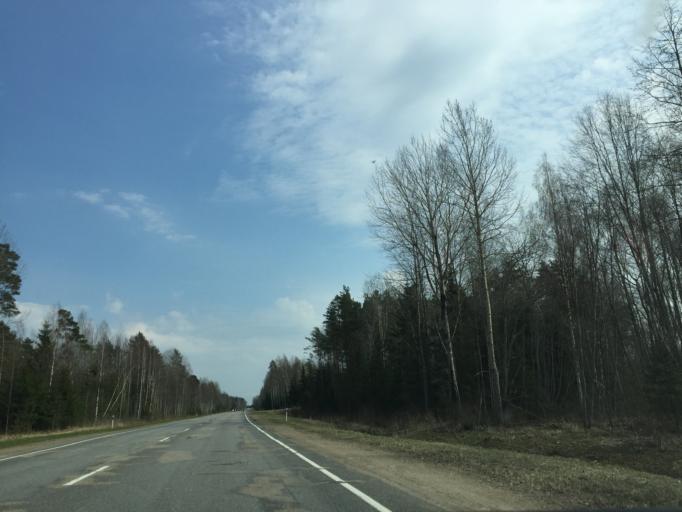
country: LV
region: Apes Novads
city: Ape
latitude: 57.4754
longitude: 26.4827
